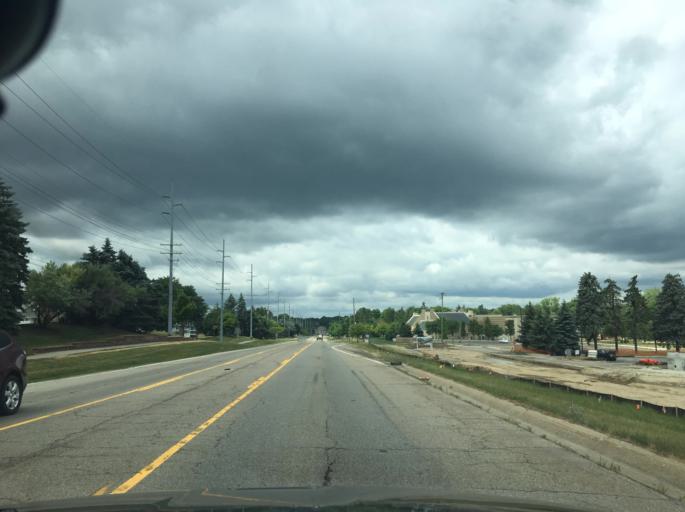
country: US
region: Michigan
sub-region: Oakland County
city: Rochester Hills
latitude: 42.6661
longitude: -83.1421
